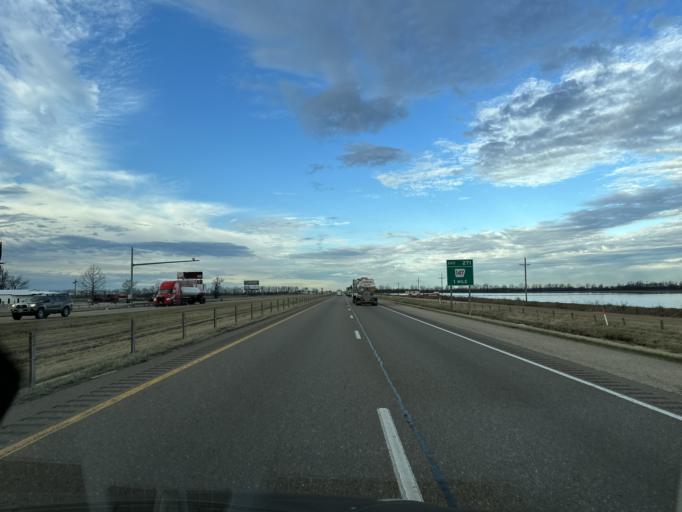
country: US
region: Arkansas
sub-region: Crittenden County
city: West Memphis
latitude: 35.1477
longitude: -90.2700
